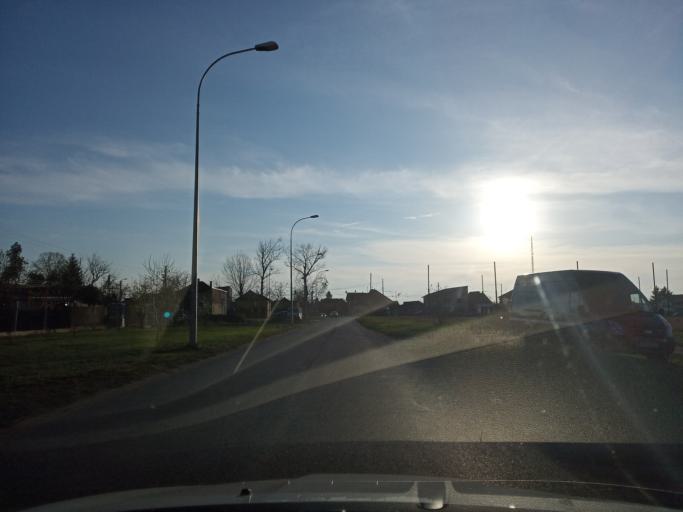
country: RO
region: Timis
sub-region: Comuna Ghiroda
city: Ghiroda
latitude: 45.7304
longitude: 21.2705
